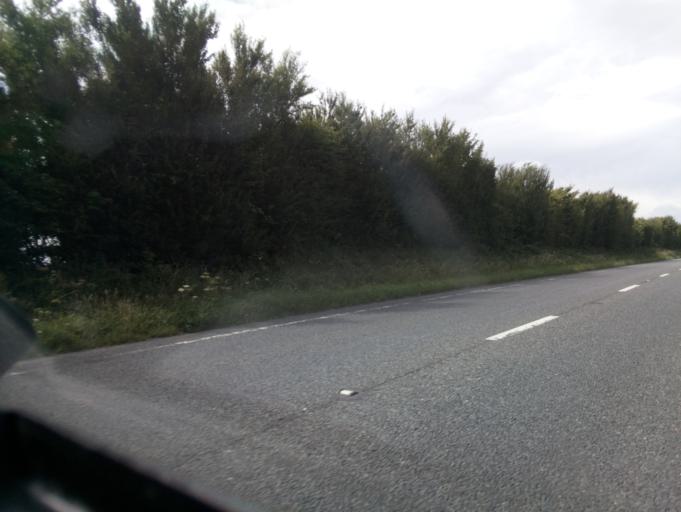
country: GB
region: England
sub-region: Dorset
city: Sherborne
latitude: 50.8120
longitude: -2.5545
